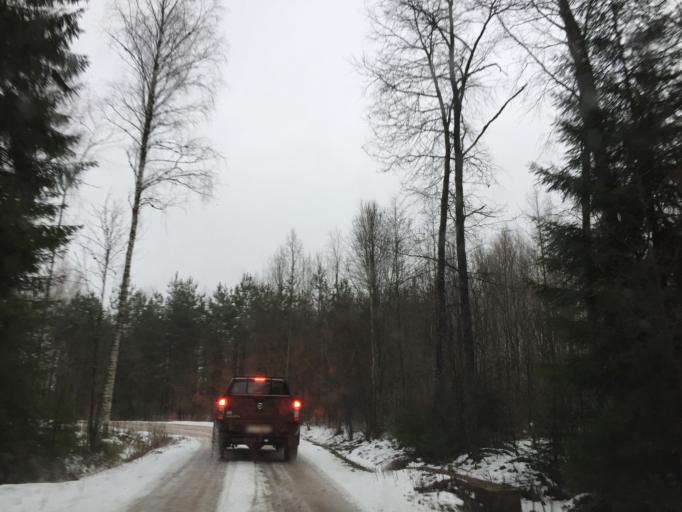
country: LV
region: Seja
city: Loja
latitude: 57.1301
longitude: 24.6047
